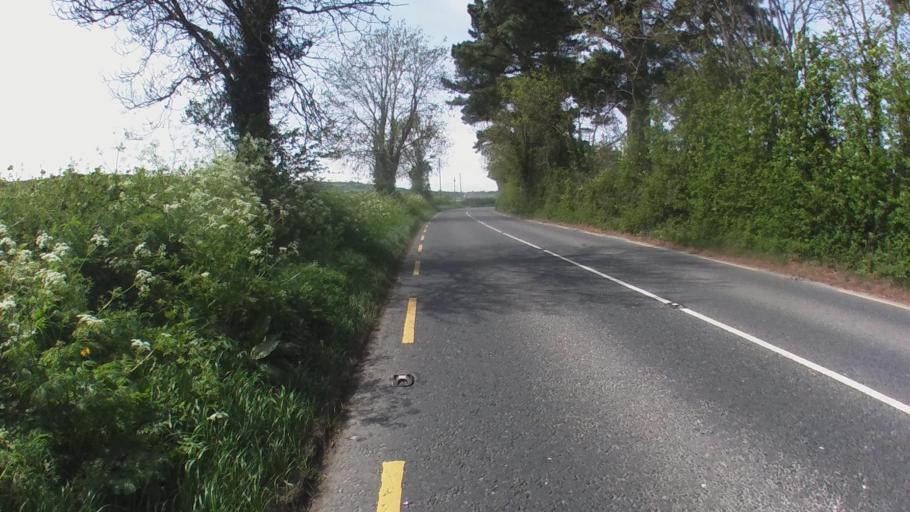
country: IE
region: Leinster
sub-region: County Carlow
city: Carlow
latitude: 52.8421
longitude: -6.9757
